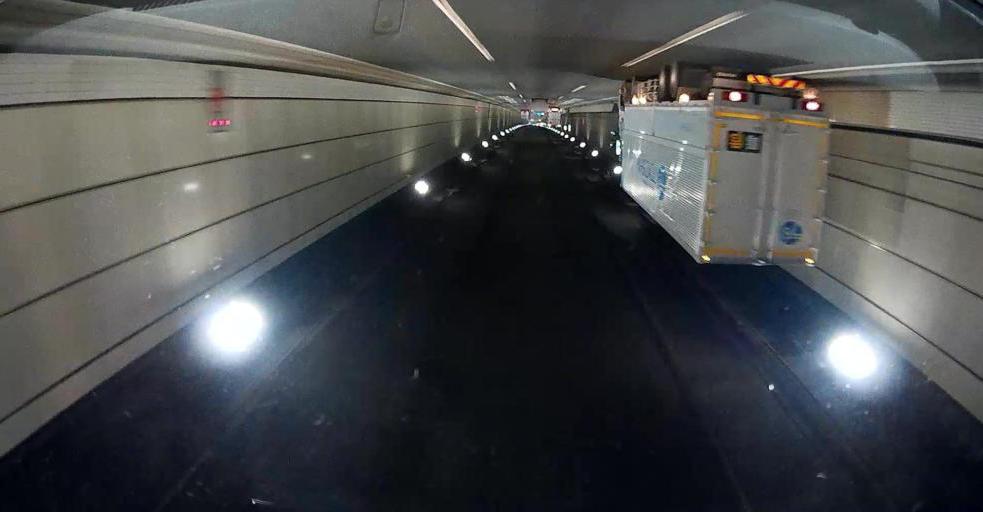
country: JP
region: Kanagawa
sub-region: Kawasaki-shi
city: Kawasaki
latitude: 35.5109
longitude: 139.7840
